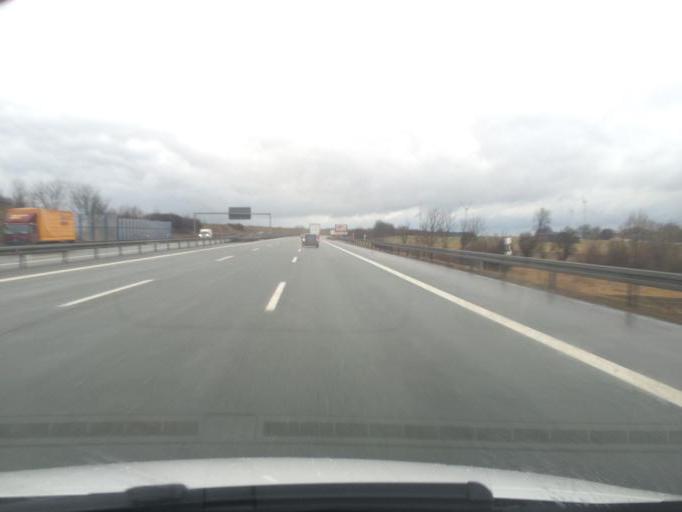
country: DE
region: Bavaria
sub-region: Upper Franconia
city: Berg
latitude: 50.3812
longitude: 11.7854
